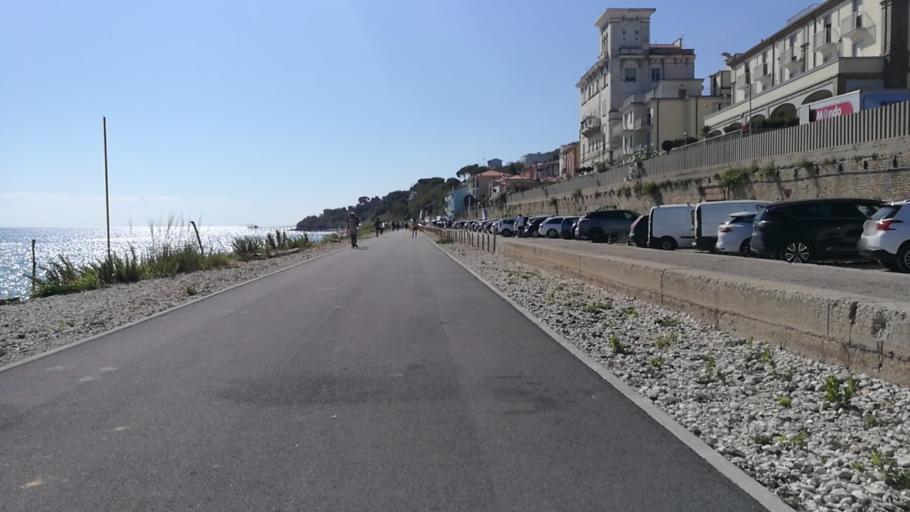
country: IT
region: Abruzzo
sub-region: Provincia di Chieti
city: Marina di San Vito
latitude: 42.3058
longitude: 14.4505
